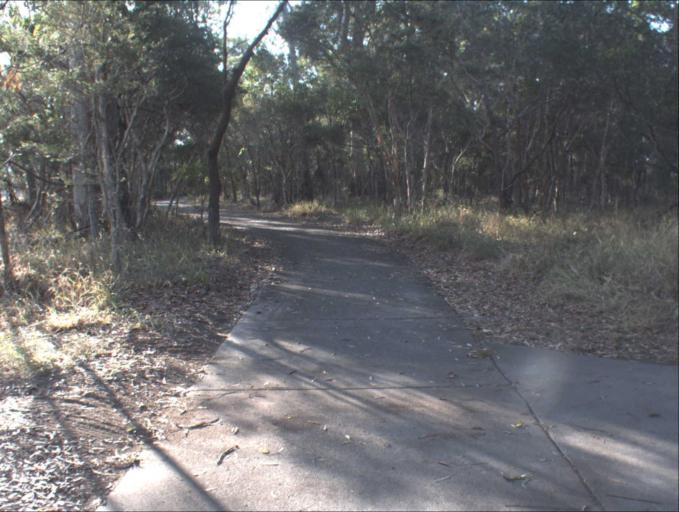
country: AU
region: Queensland
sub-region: Logan
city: Beenleigh
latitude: -27.6714
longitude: 153.2038
